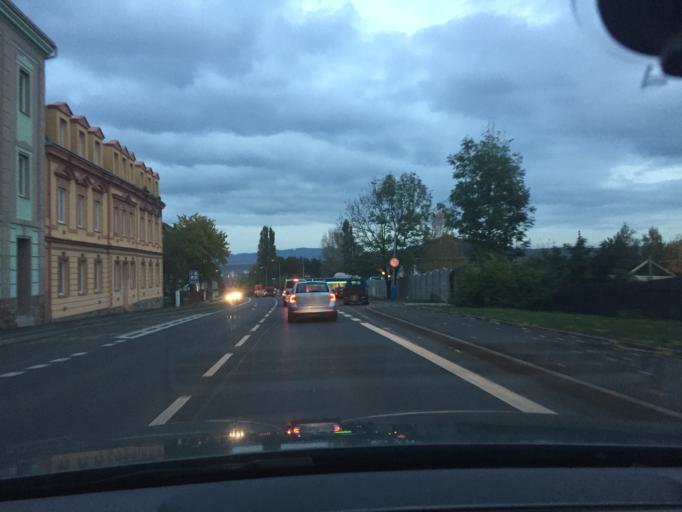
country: CZ
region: Ustecky
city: Novosedlice
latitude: 50.6561
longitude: 13.8060
